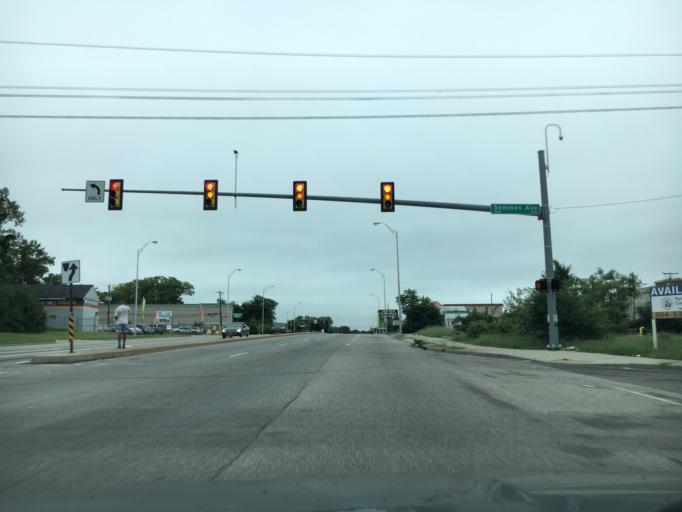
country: US
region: Virginia
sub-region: City of Richmond
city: Richmond
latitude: 37.5233
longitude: -77.4519
